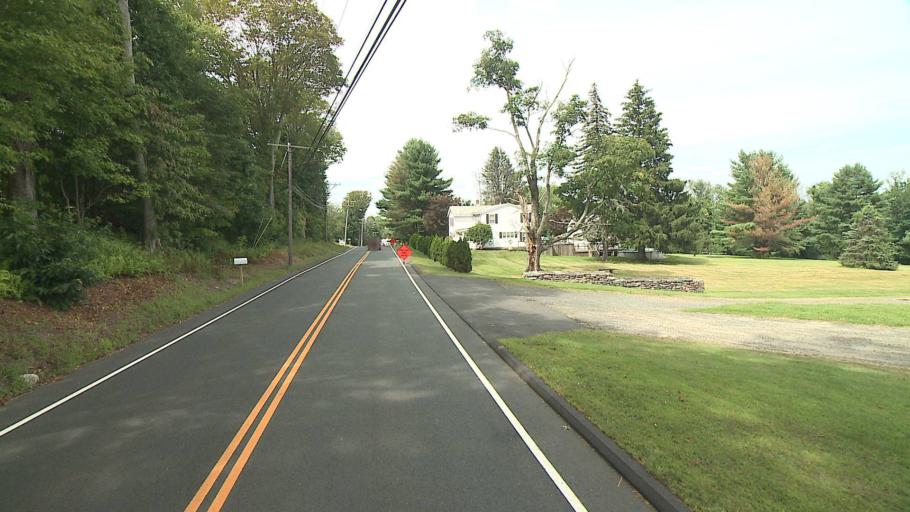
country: US
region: Connecticut
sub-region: Litchfield County
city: Plymouth
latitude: 41.6659
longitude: -73.0502
